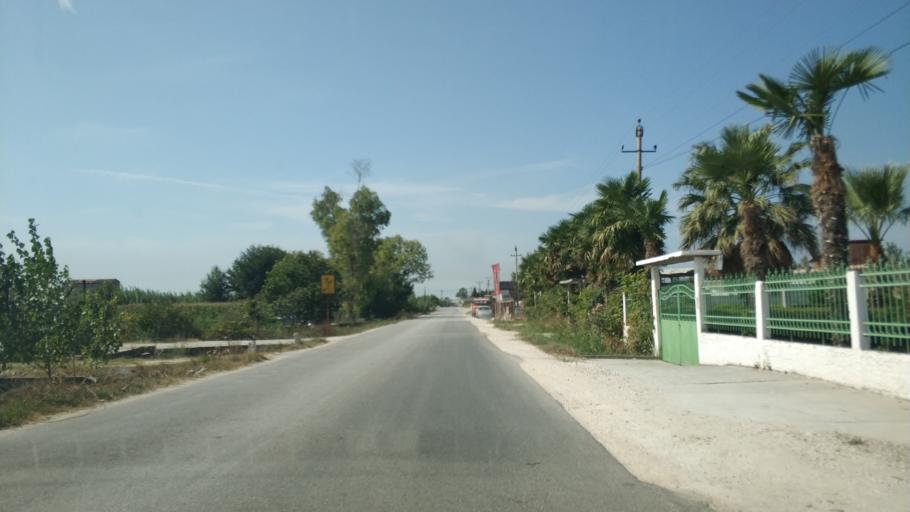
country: AL
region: Fier
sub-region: Rrethi i Fierit
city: Dermenas
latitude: 40.7406
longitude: 19.5085
